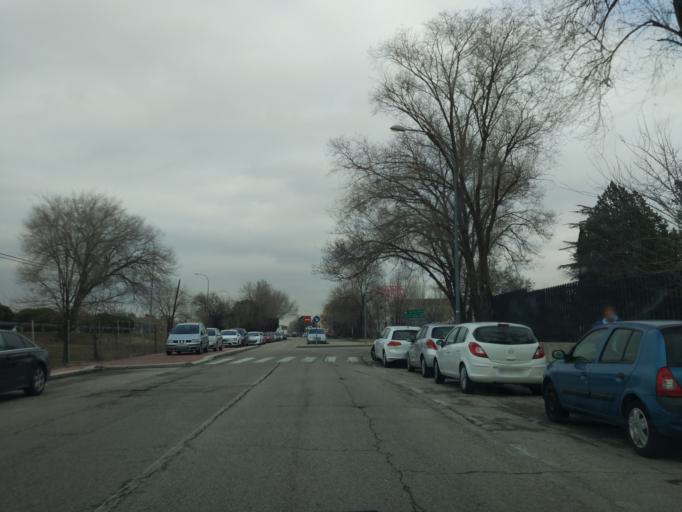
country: ES
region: Madrid
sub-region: Provincia de Madrid
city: Torrejon de Ardoz
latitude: 40.4548
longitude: -3.5062
